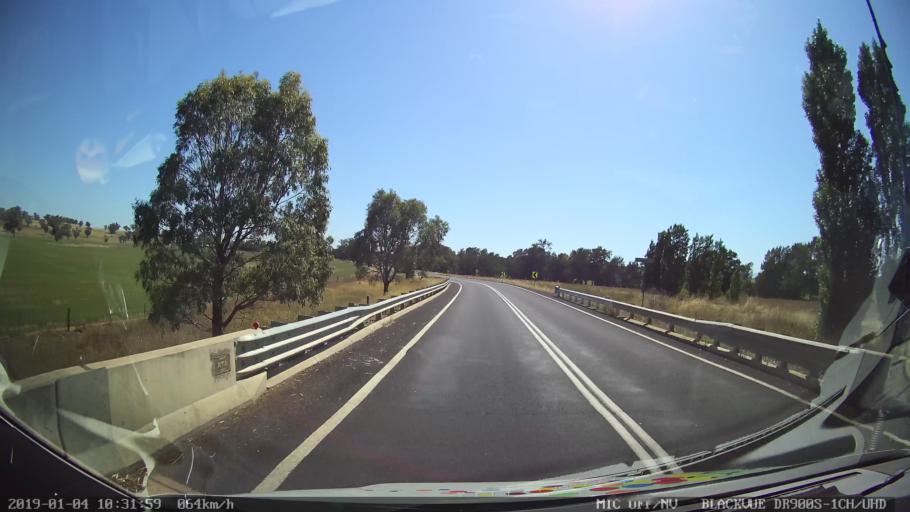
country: AU
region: New South Wales
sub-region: Cabonne
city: Canowindra
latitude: -33.3300
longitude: 148.6352
